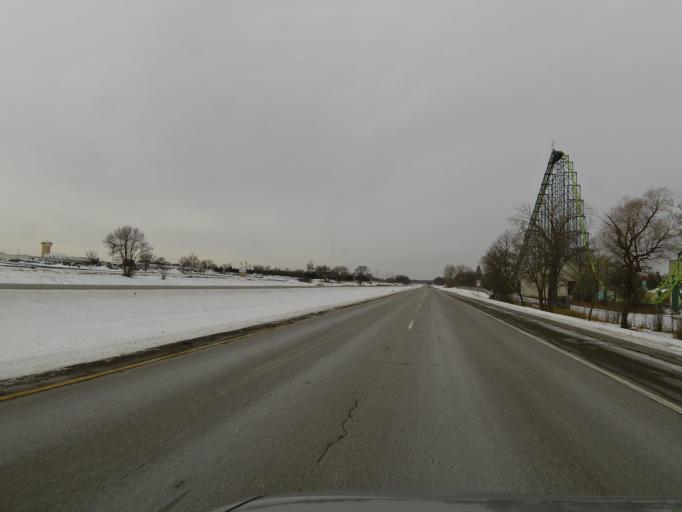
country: US
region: Minnesota
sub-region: Hennepin County
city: Eden Prairie
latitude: 44.7972
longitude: -93.4546
